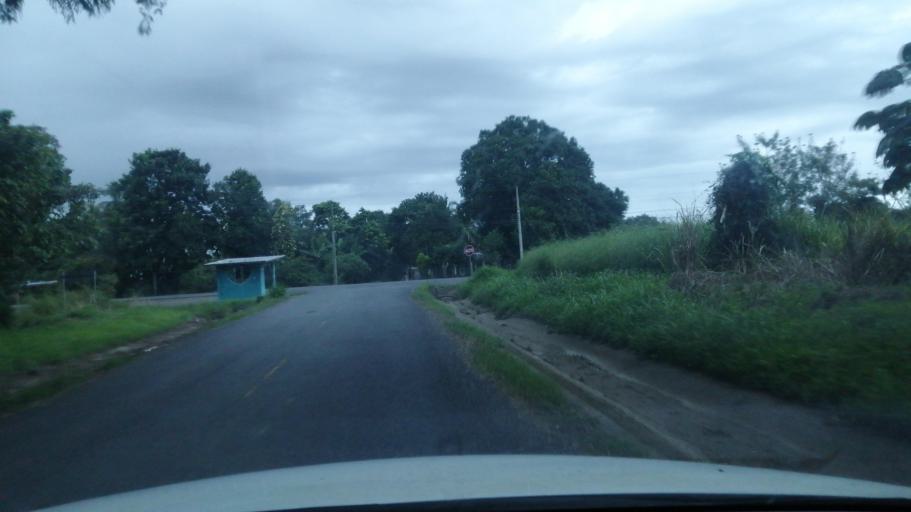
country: PA
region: Chiriqui
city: Alanje
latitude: 8.3954
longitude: -82.4959
